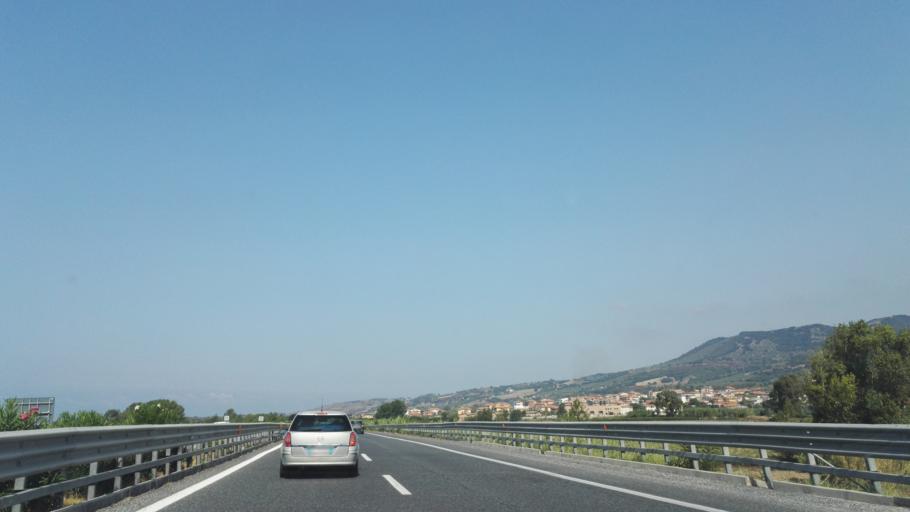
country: IT
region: Calabria
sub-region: Provincia di Catanzaro
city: Santa Eufemia Lamezia
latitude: 38.9343
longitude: 16.2199
